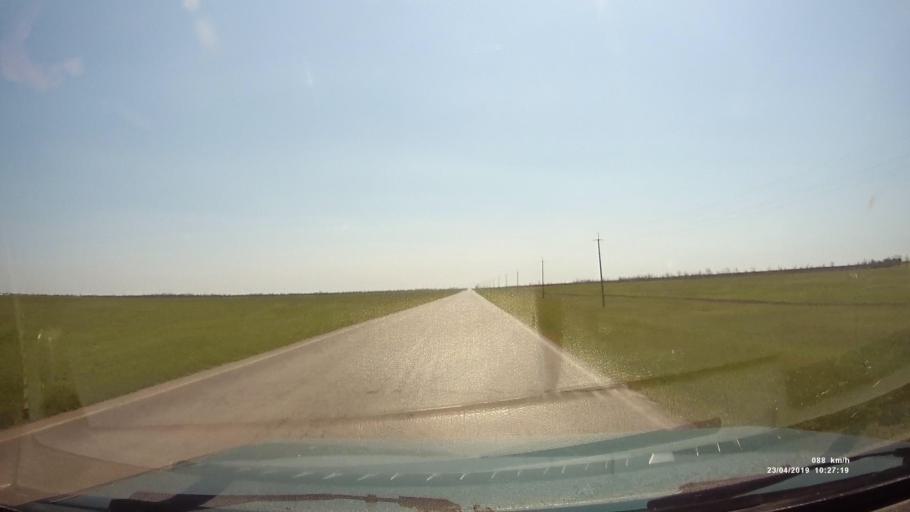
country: RU
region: Kalmykiya
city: Yashalta
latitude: 46.6147
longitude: 42.4892
